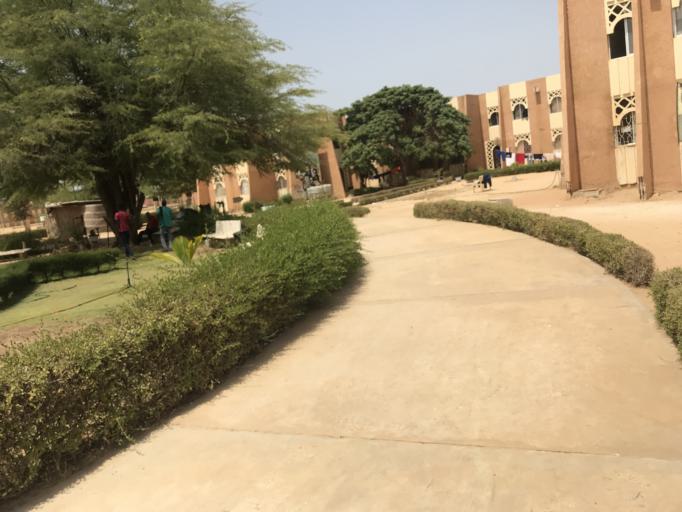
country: SN
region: Saint-Louis
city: Saint-Louis
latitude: 16.0636
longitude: -16.4257
